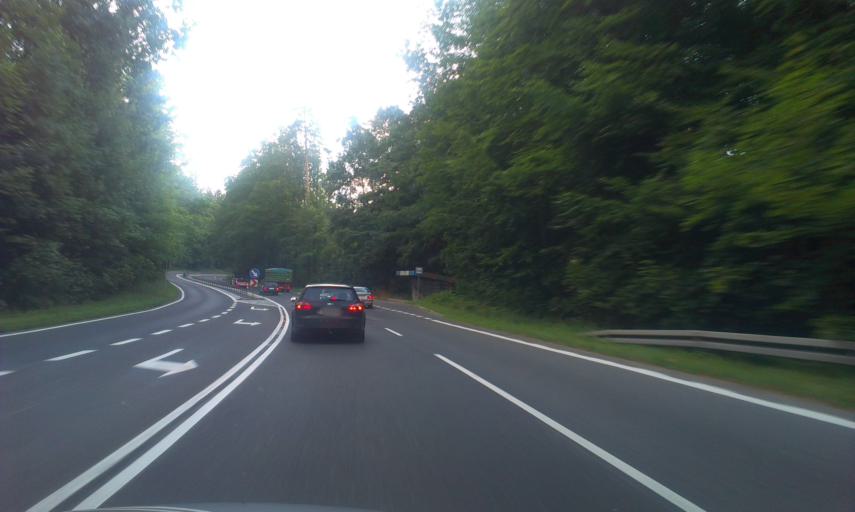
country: PL
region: West Pomeranian Voivodeship
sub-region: Koszalin
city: Koszalin
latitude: 54.2185
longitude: 16.2234
